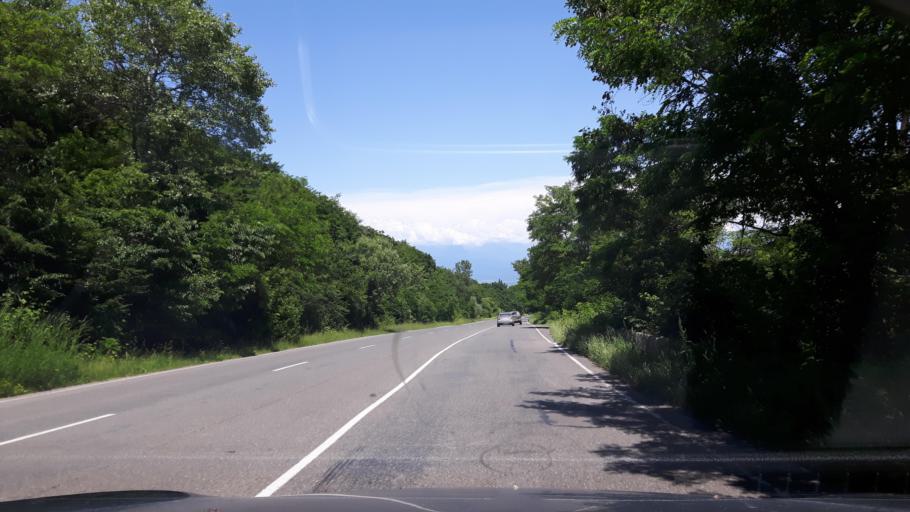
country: GE
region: Kakheti
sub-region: Gurjaani
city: Gurjaani
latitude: 41.6805
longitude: 45.8425
